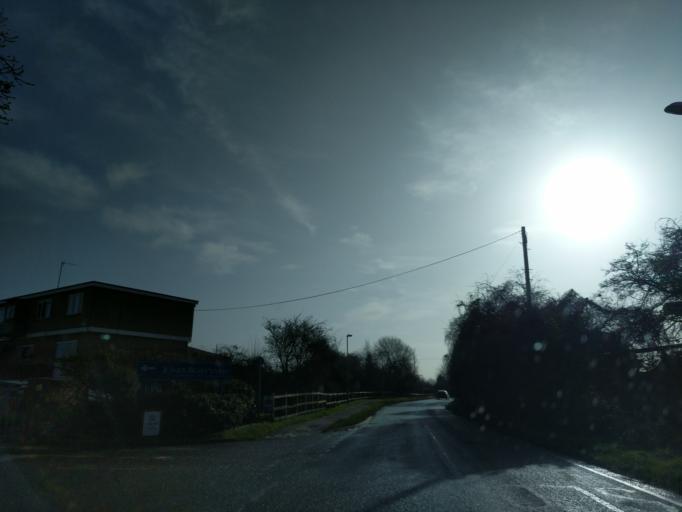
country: GB
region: England
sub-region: Cambridgeshire
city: Hemingford Grey
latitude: 52.3165
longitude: -0.0777
